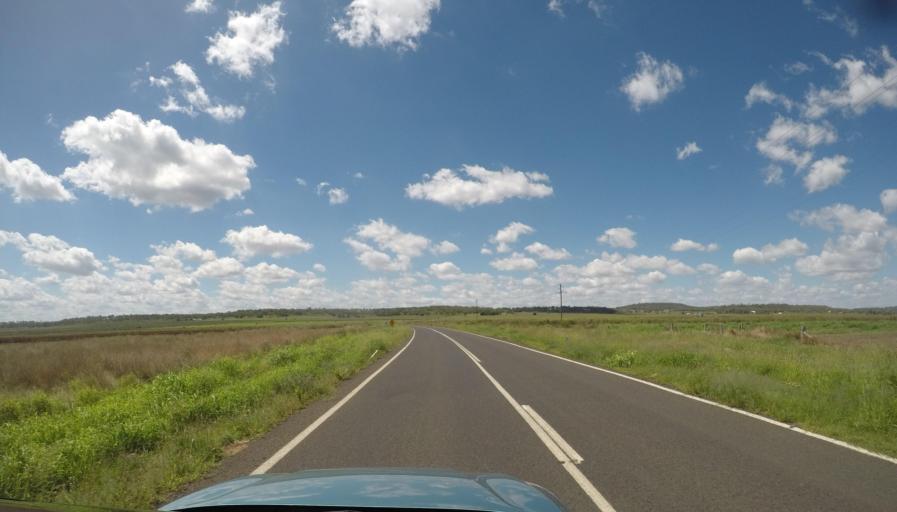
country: AU
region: Queensland
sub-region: Toowoomba
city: Oakey
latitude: -27.5414
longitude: 151.6500
